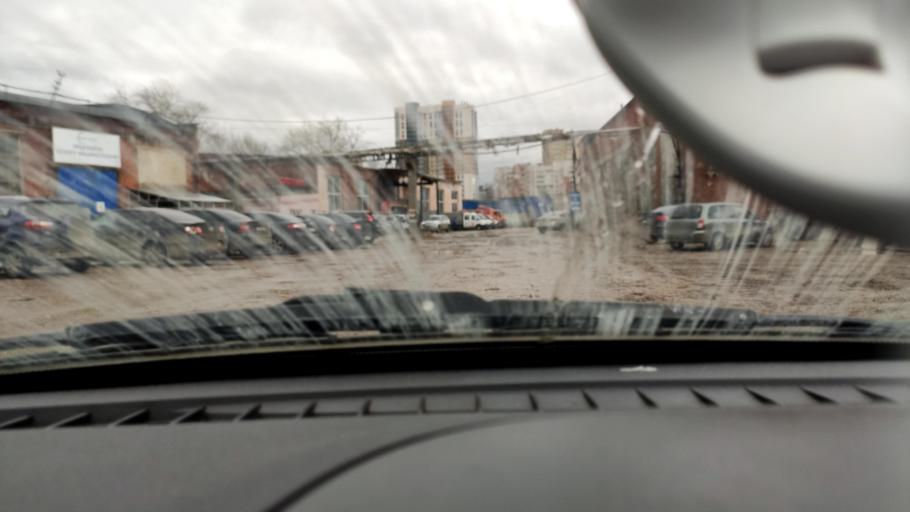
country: RU
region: Perm
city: Kondratovo
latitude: 58.0031
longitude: 56.1463
